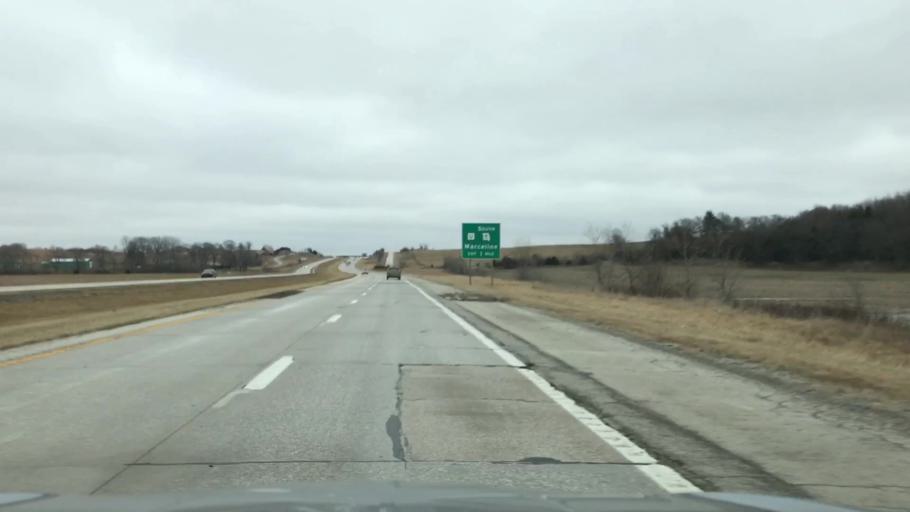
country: US
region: Missouri
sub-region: Linn County
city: Marceline
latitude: 39.7609
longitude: -92.9662
